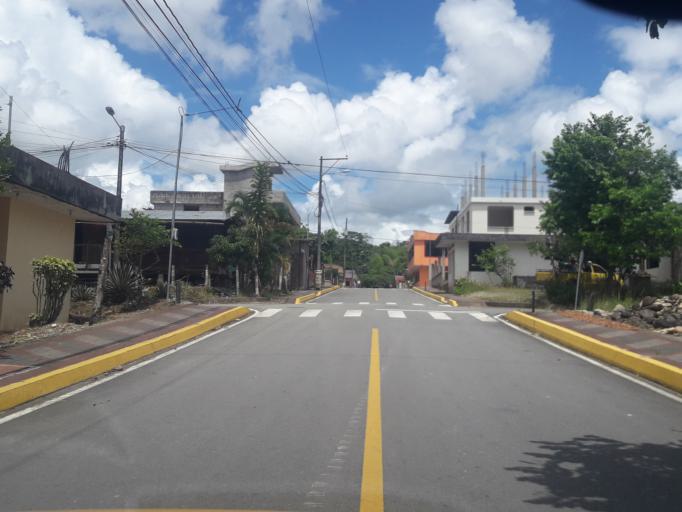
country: EC
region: Napo
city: Tena
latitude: -1.0087
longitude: -77.8124
